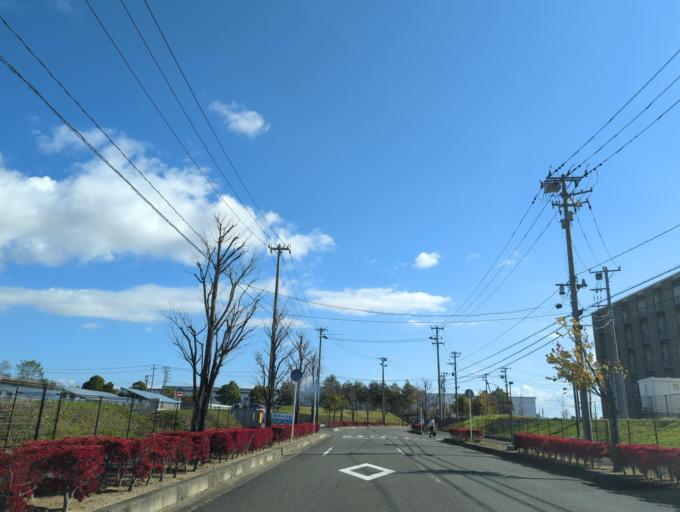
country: JP
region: Fukushima
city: Koriyama
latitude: 37.4493
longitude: 140.3135
